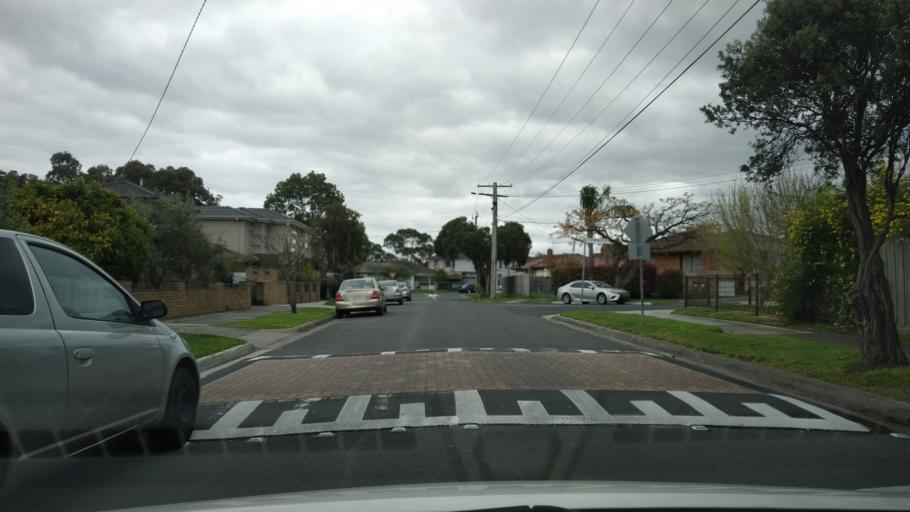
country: AU
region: Victoria
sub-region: Greater Dandenong
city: Noble Park
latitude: -37.9676
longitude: 145.1812
